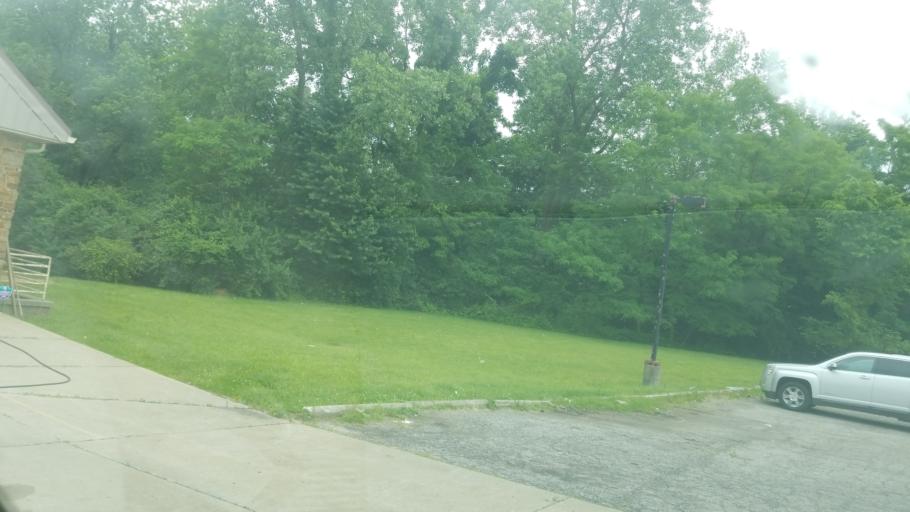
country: US
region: Ohio
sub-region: Richland County
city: Mansfield
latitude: 40.7199
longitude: -82.5435
